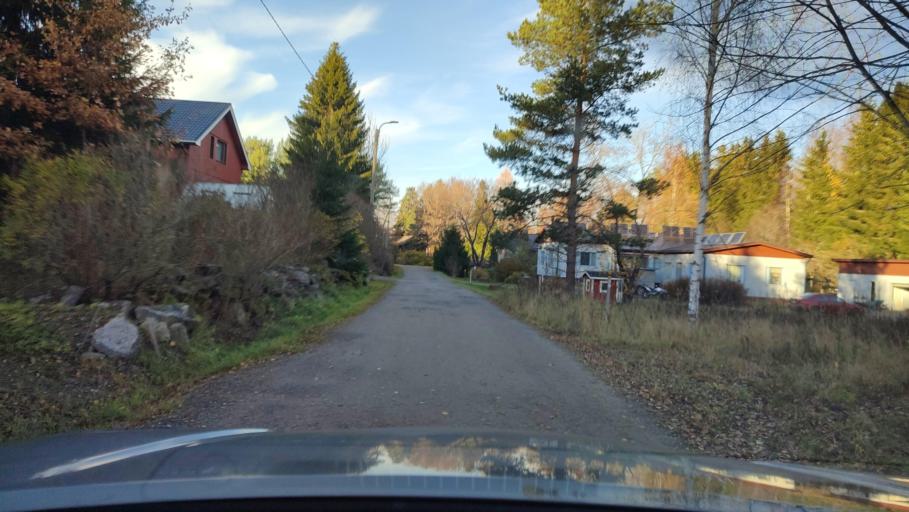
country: FI
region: Ostrobothnia
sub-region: Vaasa
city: Teeriniemi
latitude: 63.0689
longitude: 21.6952
